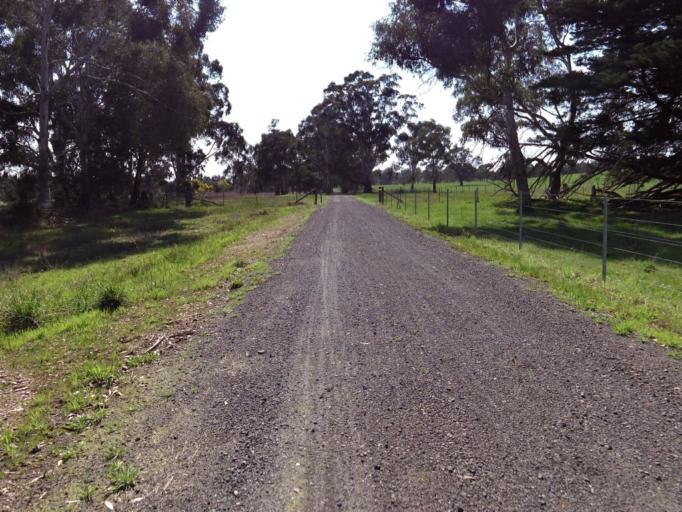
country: AU
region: Victoria
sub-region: Murrindindi
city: Alexandra
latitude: -37.1243
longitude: 145.5996
